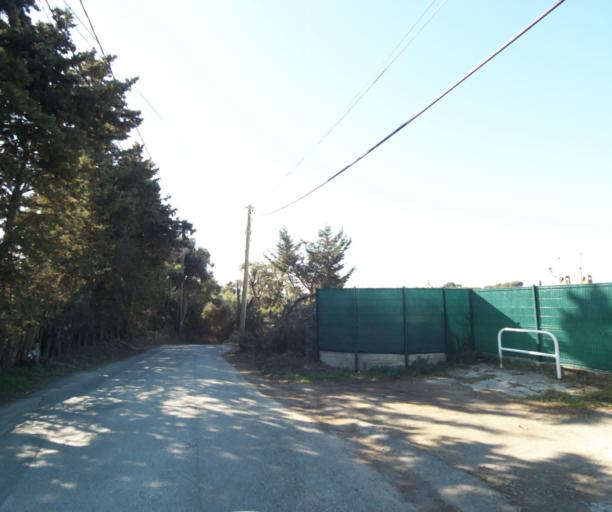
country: FR
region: Provence-Alpes-Cote d'Azur
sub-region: Departement des Alpes-Maritimes
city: Biot
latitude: 43.6062
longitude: 7.1020
